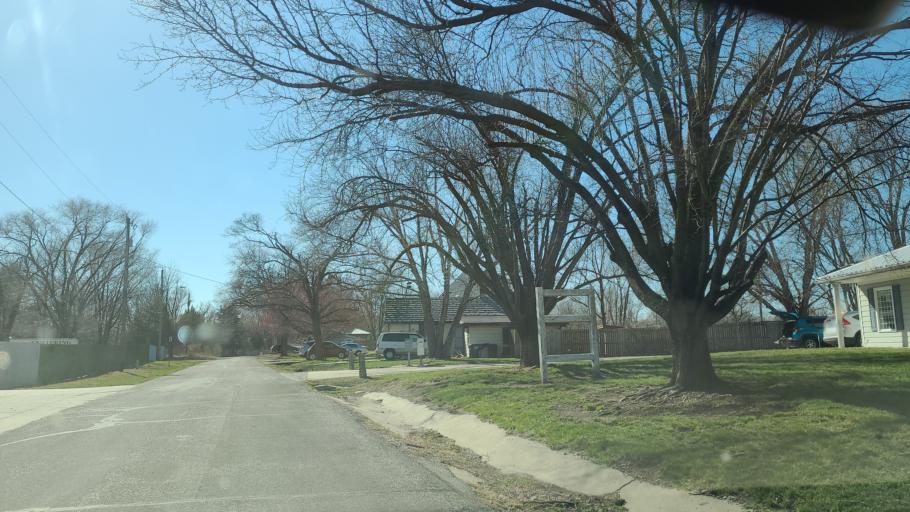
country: US
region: Kansas
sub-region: Douglas County
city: Lawrence
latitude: 38.9798
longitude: -95.2211
